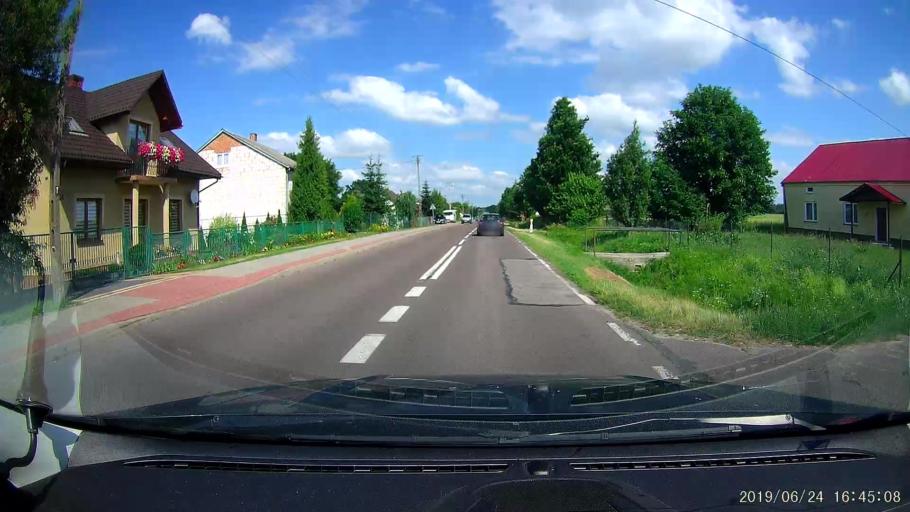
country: PL
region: Lublin Voivodeship
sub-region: Powiat tomaszowski
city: Michalow
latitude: 50.5329
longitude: 23.6635
